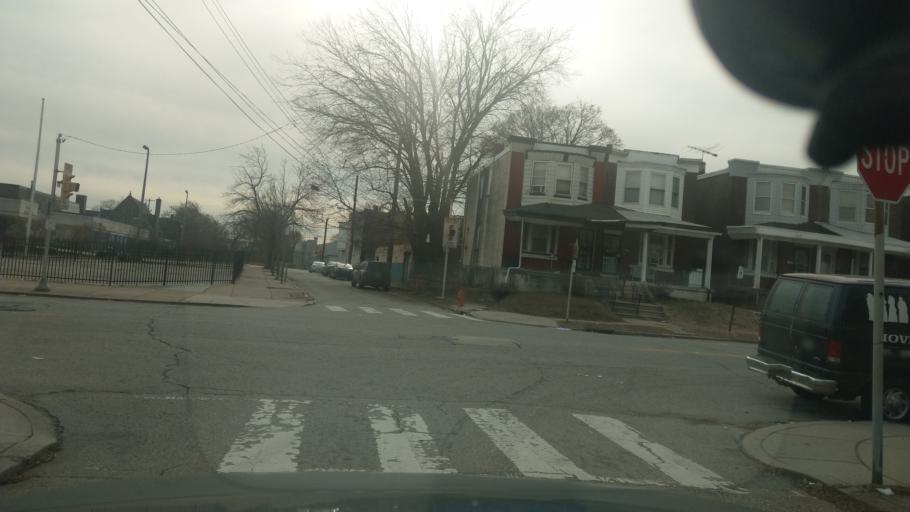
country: US
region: Pennsylvania
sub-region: Montgomery County
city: Wyncote
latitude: 40.0486
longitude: -75.1499
